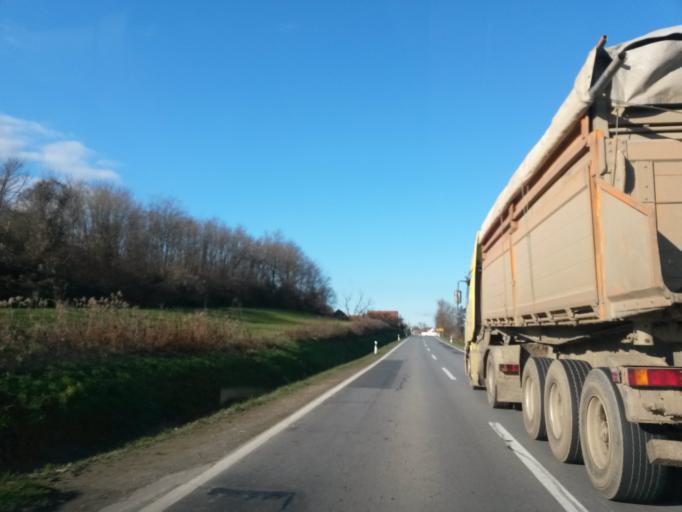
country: HR
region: Virovitick-Podravska
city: Slatina
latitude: 45.7366
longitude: 17.6167
